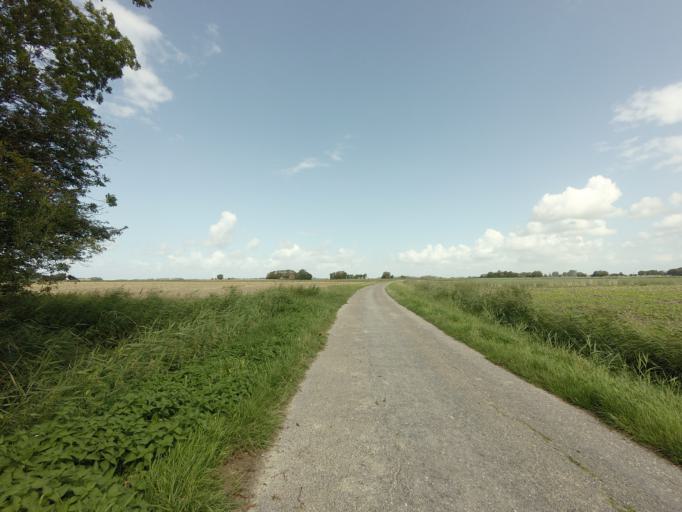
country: NL
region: Friesland
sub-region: Gemeente Harlingen
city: Harlingen
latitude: 53.1180
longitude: 5.4380
